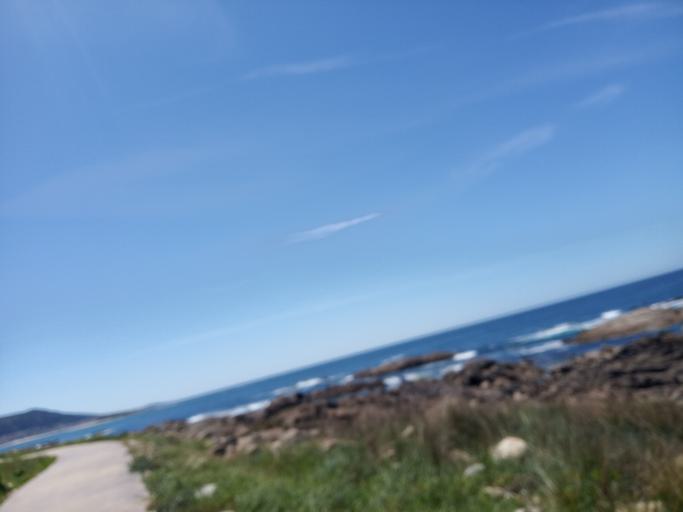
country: ES
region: Galicia
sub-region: Provincia de Pontevedra
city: A Guarda
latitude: 41.8758
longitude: -8.8765
